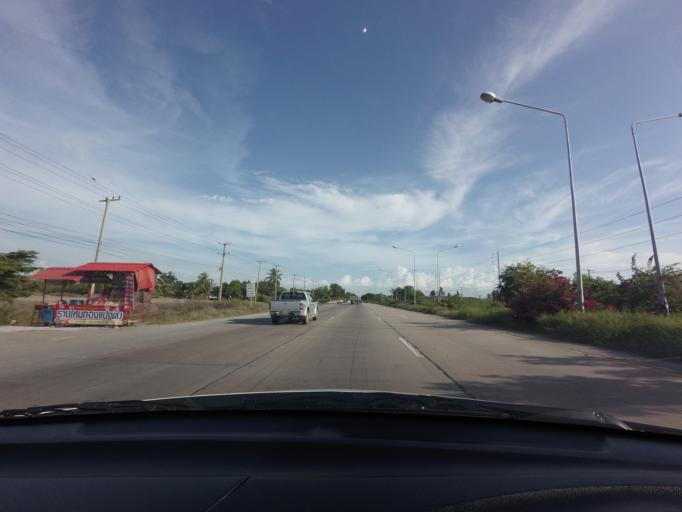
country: TH
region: Phra Nakhon Si Ayutthaya
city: Lat Bua Luang
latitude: 14.1550
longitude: 100.2909
